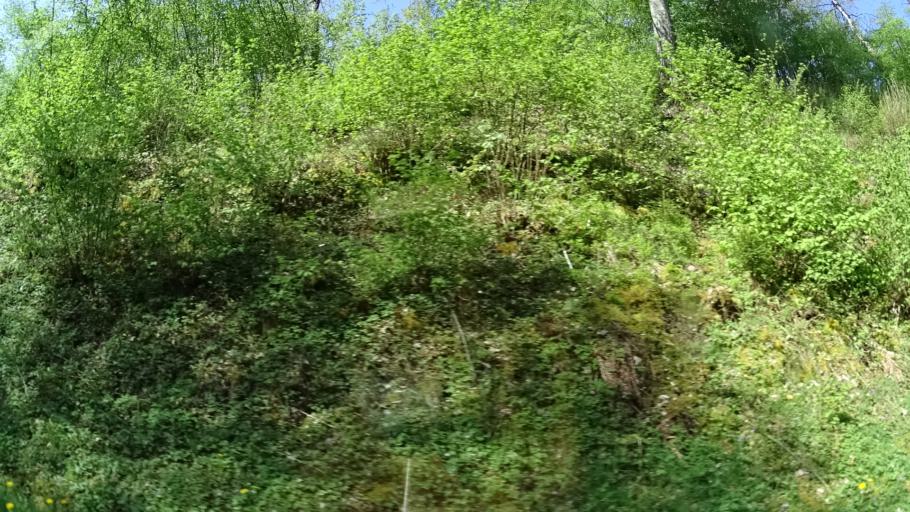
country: DE
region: Baden-Wuerttemberg
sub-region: Karlsruhe Region
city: Hofen an der Enz
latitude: 48.7979
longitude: 8.5533
